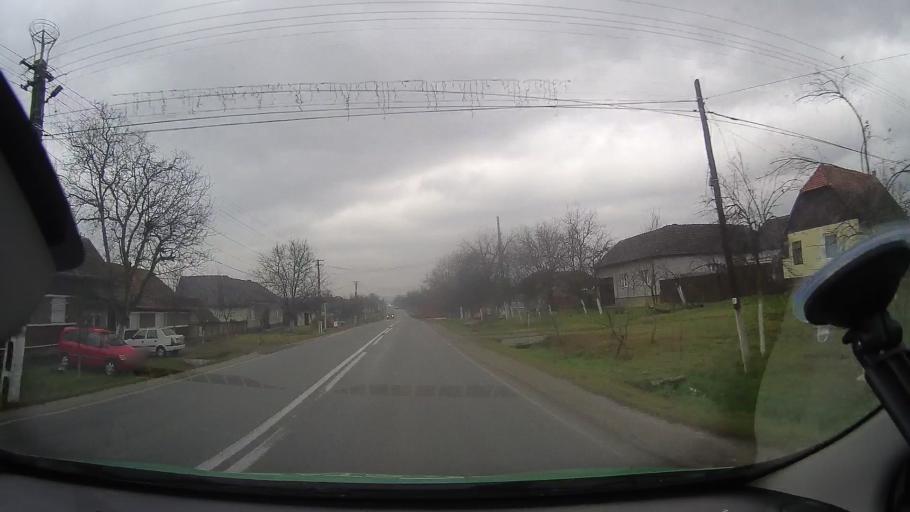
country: RO
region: Arad
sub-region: Comuna Almas
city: Almas
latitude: 46.2897
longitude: 22.2247
